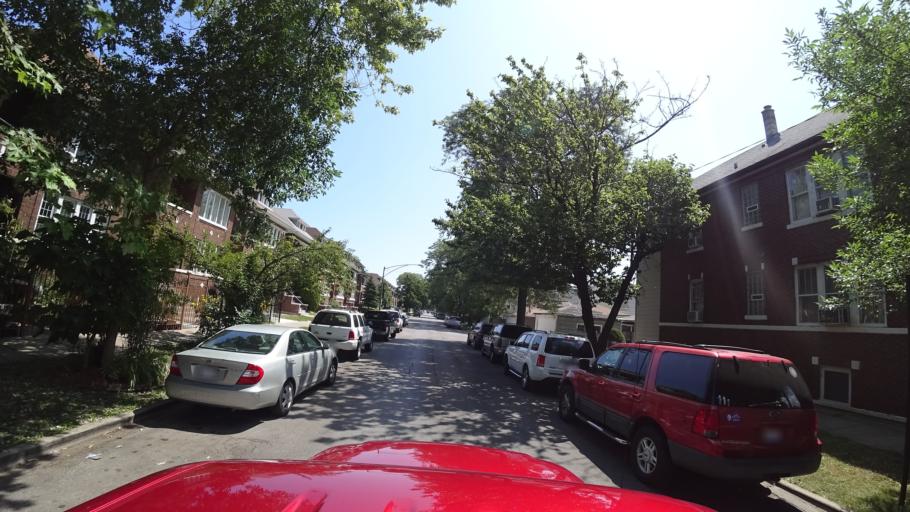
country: US
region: Illinois
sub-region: Cook County
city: Chicago
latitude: 41.8175
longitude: -87.6932
